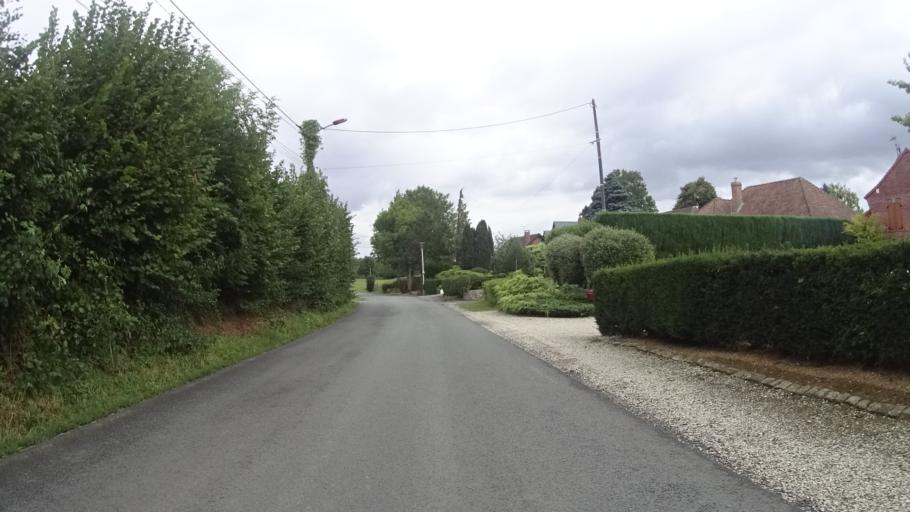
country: FR
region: Nord-Pas-de-Calais
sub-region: Departement du Nord
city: Berlaimont
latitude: 50.1828
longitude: 3.8076
